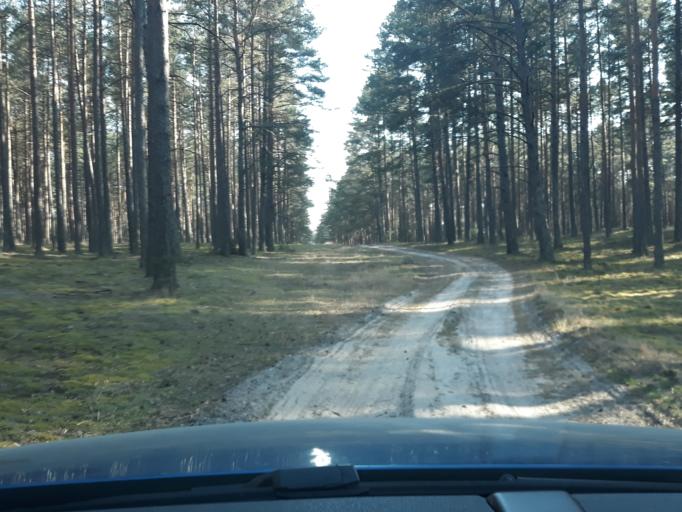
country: PL
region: Pomeranian Voivodeship
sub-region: Powiat bytowski
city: Lipnica
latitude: 53.9009
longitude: 17.4954
